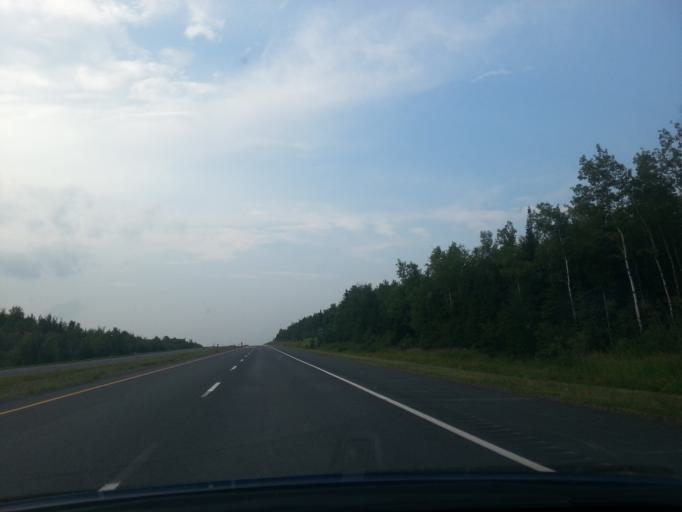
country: CA
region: New Brunswick
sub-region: Madawaska County
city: Saint-Leonard
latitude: 47.1559
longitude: -67.9068
